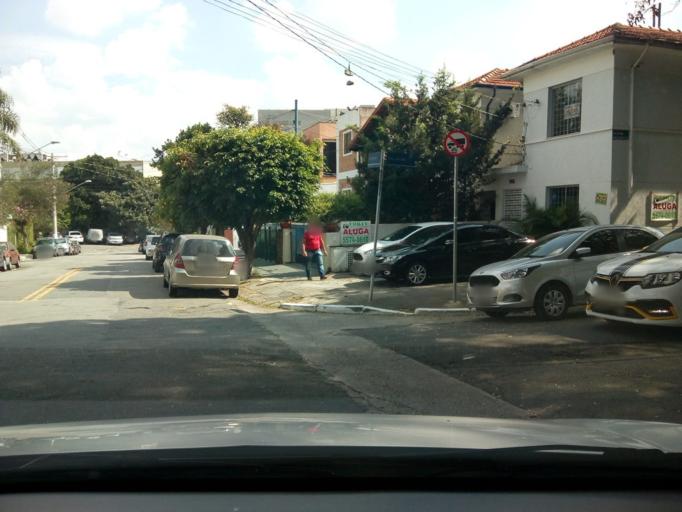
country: BR
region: Sao Paulo
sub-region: Sao Paulo
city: Sao Paulo
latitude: -23.5840
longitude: -46.6495
